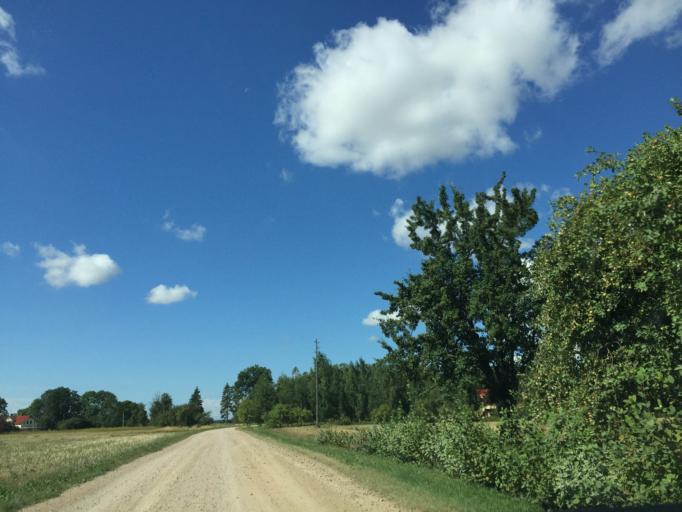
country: LV
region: Bauskas Rajons
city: Bauska
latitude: 56.4231
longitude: 24.1794
